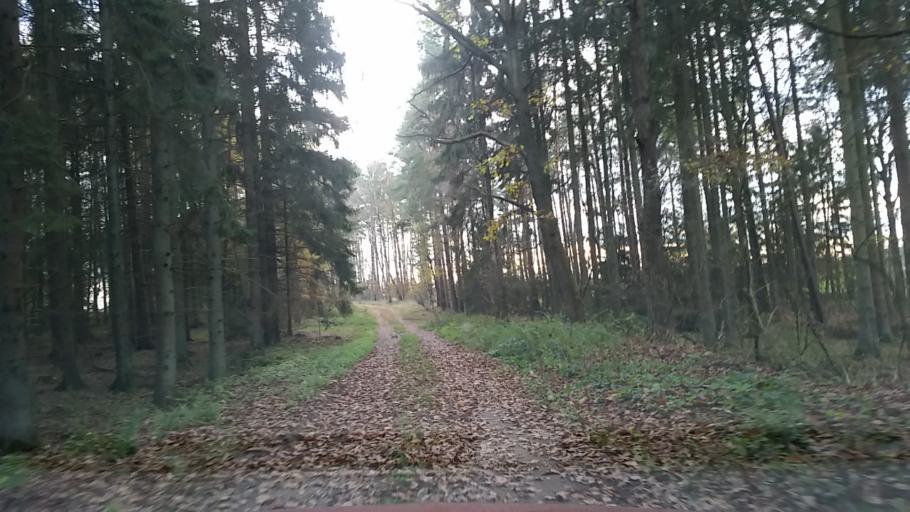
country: DE
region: Lower Saxony
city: Sprakensehl
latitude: 52.7965
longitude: 10.5108
